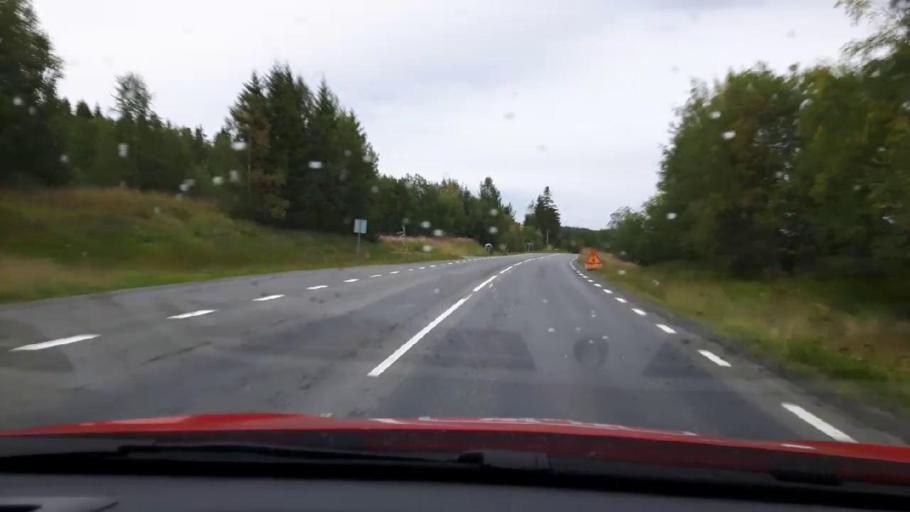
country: SE
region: Jaemtland
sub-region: Are Kommun
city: Jarpen
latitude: 63.3845
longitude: 13.4172
